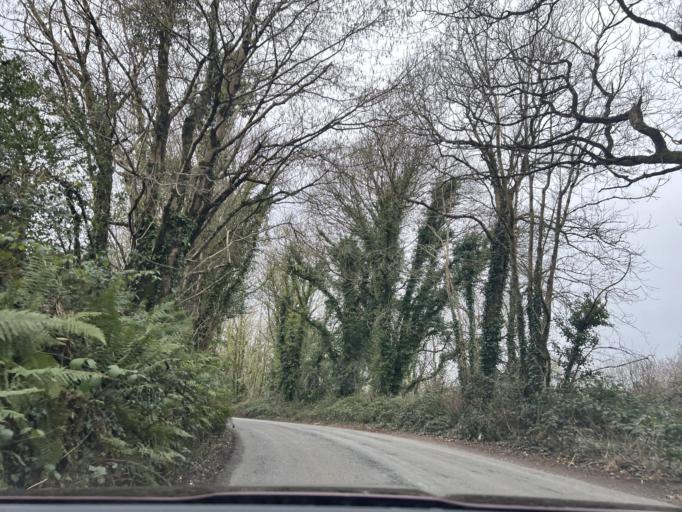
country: IE
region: Leinster
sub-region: Loch Garman
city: Castlebridge
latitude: 52.3809
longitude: -6.5400
